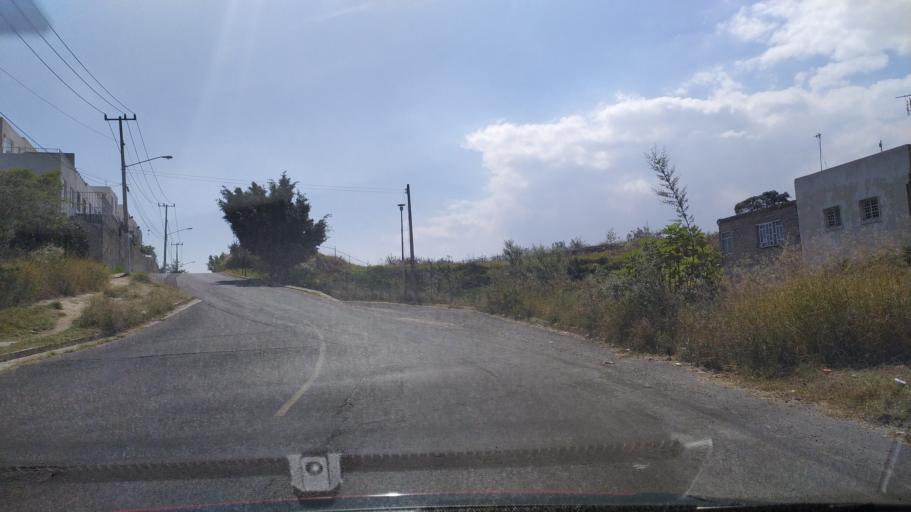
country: MX
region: Jalisco
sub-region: Zapopan
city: Campo Real
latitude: 20.7754
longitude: -103.4343
